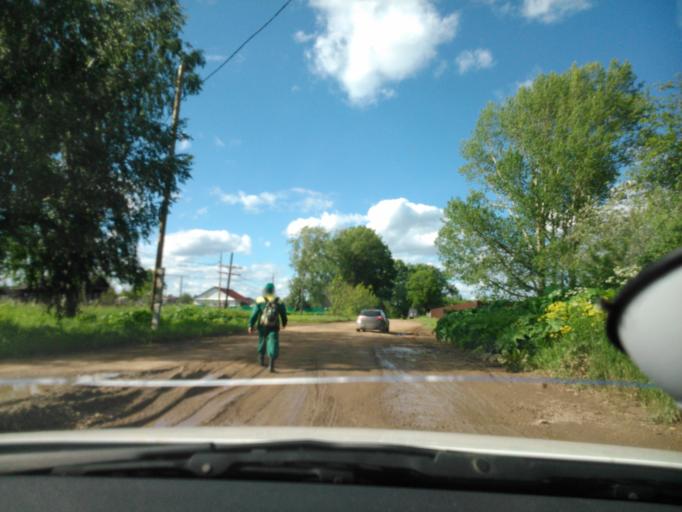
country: RU
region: Perm
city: Ust'-Kachka
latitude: 57.9435
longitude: 55.7440
